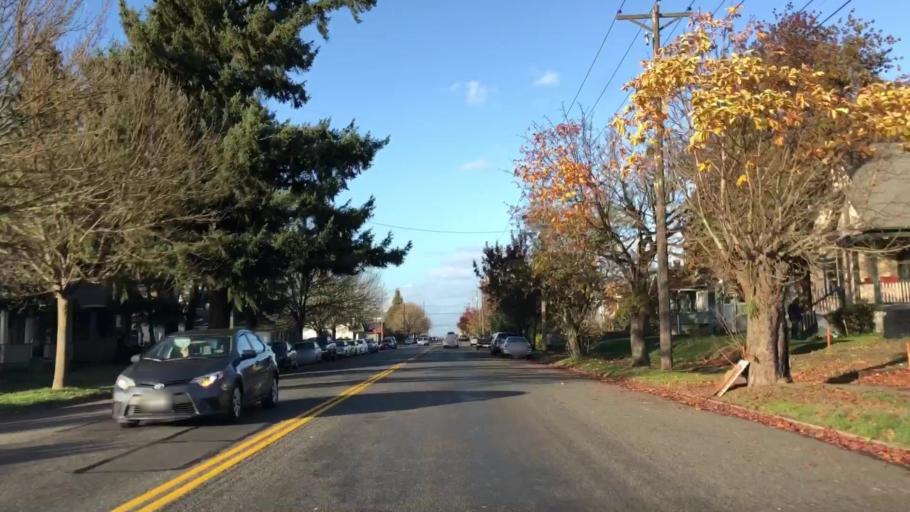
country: US
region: Washington
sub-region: Pierce County
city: Tacoma
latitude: 47.2171
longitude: -122.4508
